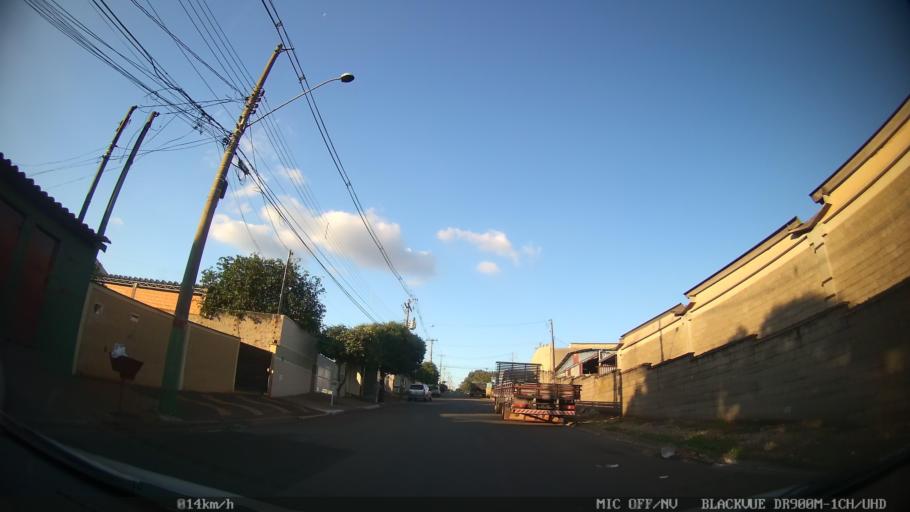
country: BR
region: Sao Paulo
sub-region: Santa Barbara D'Oeste
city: Santa Barbara d'Oeste
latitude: -22.7490
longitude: -47.3778
